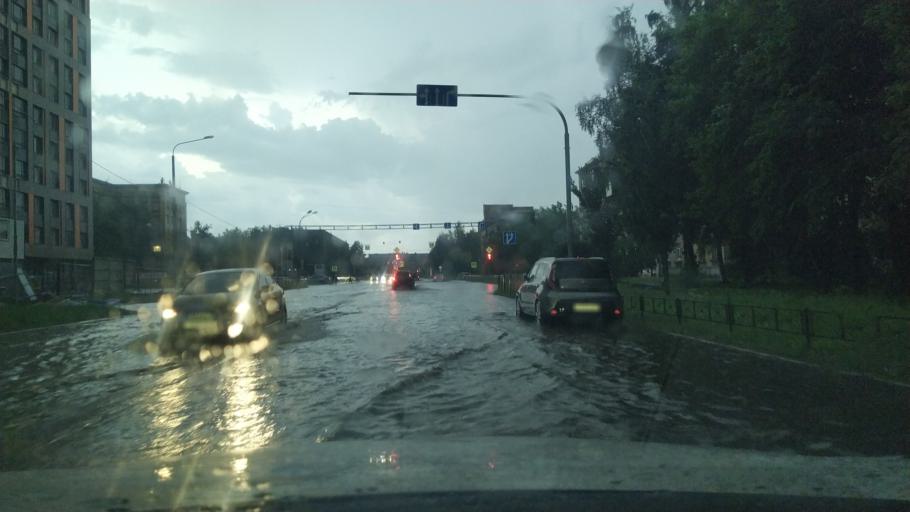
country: RU
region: Leningrad
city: Sampsonievskiy
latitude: 59.9823
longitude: 30.3535
